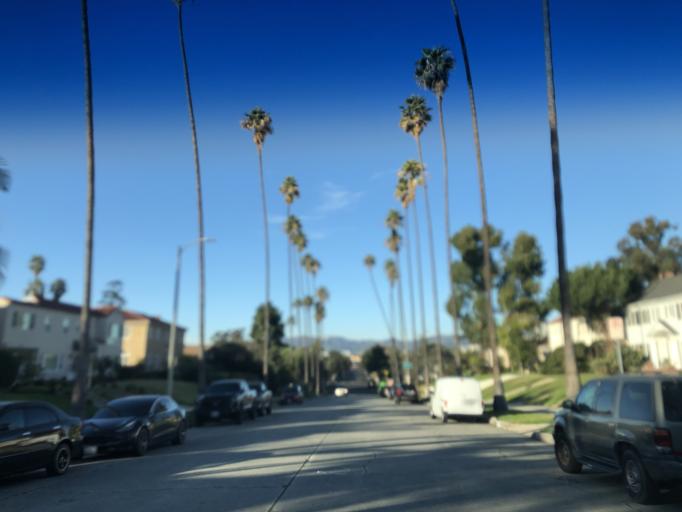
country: US
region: California
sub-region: Los Angeles County
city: Hollywood
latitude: 34.0481
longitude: -118.3145
